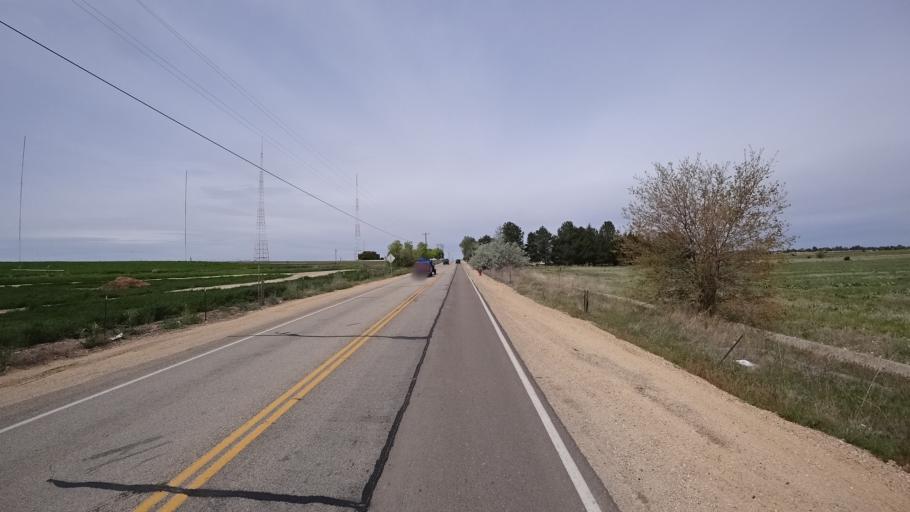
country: US
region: Idaho
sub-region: Ada County
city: Meridian
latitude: 43.5609
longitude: -116.3959
